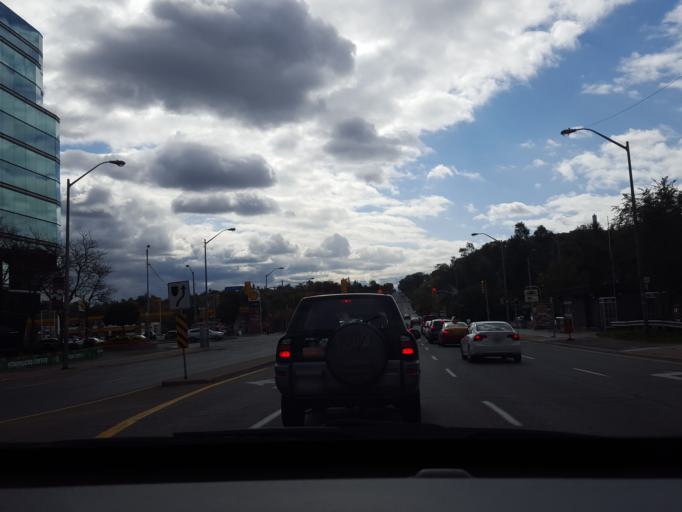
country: CA
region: Ontario
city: Willowdale
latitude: 43.7449
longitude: -79.4070
